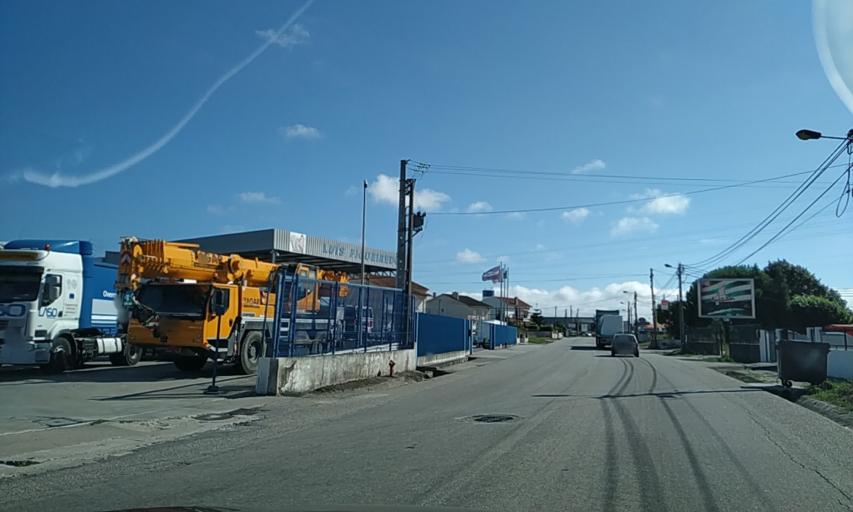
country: PT
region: Aveiro
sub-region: Aveiro
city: Aveiro
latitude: 40.6715
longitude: -8.6054
